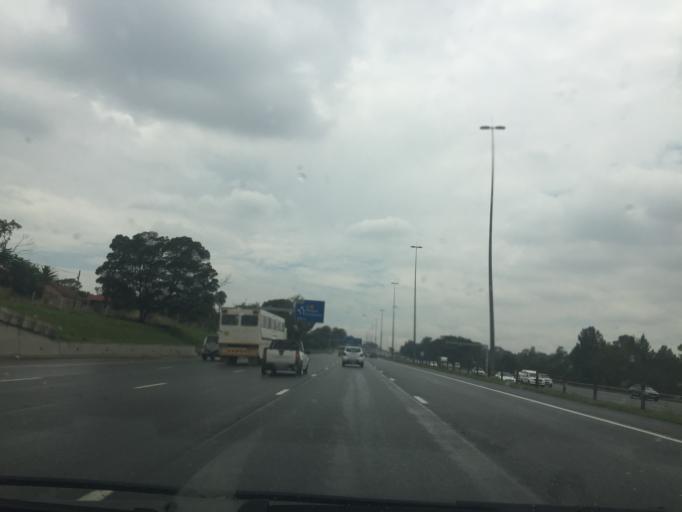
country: ZA
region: Gauteng
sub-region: City of Johannesburg Metropolitan Municipality
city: Midrand
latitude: -26.0410
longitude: 28.0783
